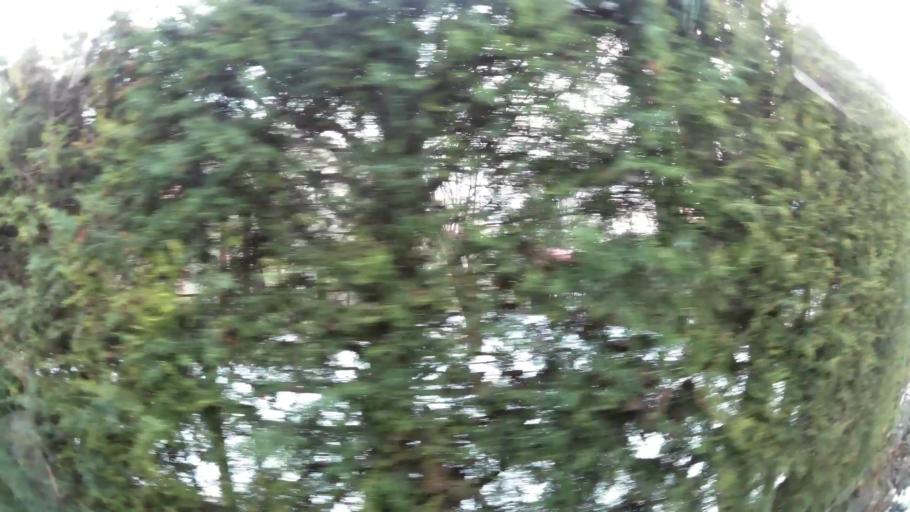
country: MK
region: Butel
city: Butel
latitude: 42.0224
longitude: 21.4475
